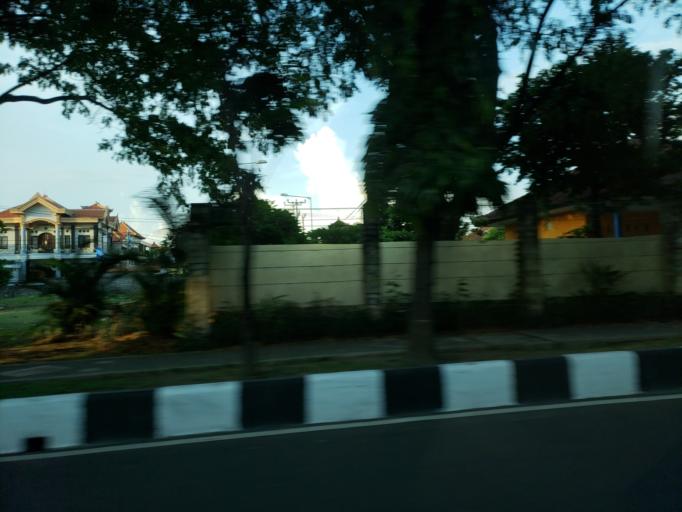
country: ID
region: Bali
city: Kelanabian
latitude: -8.7438
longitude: 115.1763
